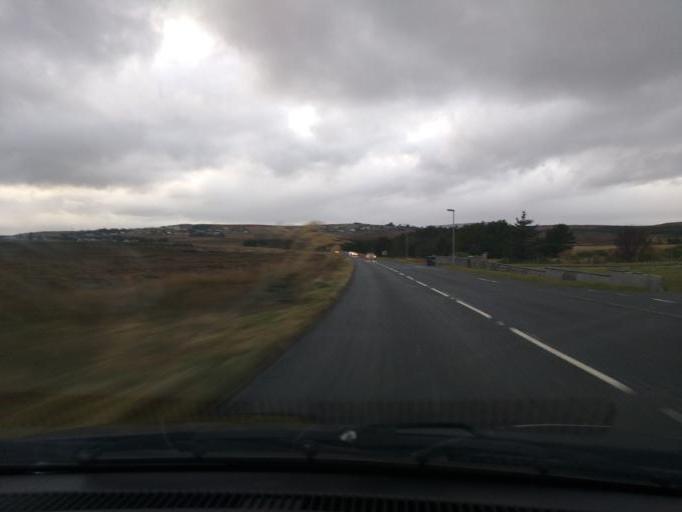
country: GB
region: Scotland
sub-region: Eilean Siar
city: Isle of Lewis
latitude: 58.2446
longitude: -6.3602
